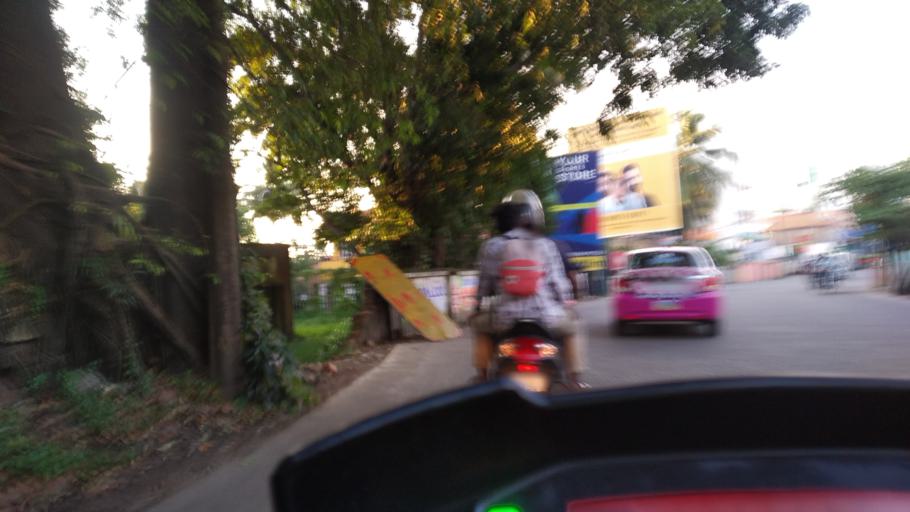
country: IN
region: Kerala
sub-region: Ernakulam
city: Cochin
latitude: 9.9612
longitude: 76.3213
